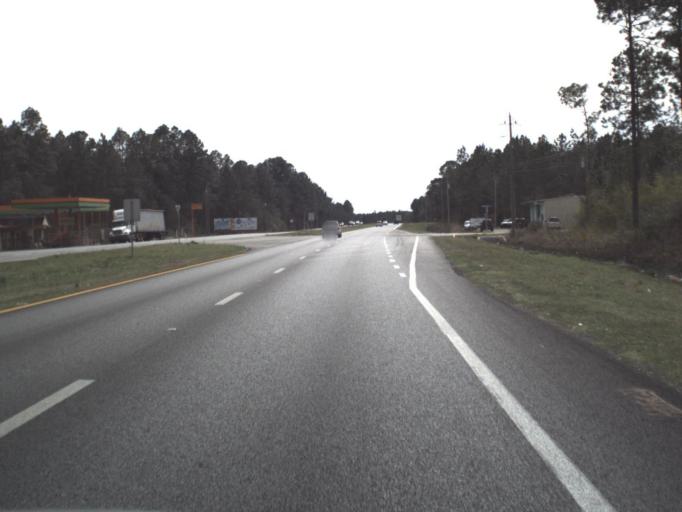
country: US
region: Florida
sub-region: Bay County
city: Youngstown
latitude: 30.4077
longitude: -85.4320
